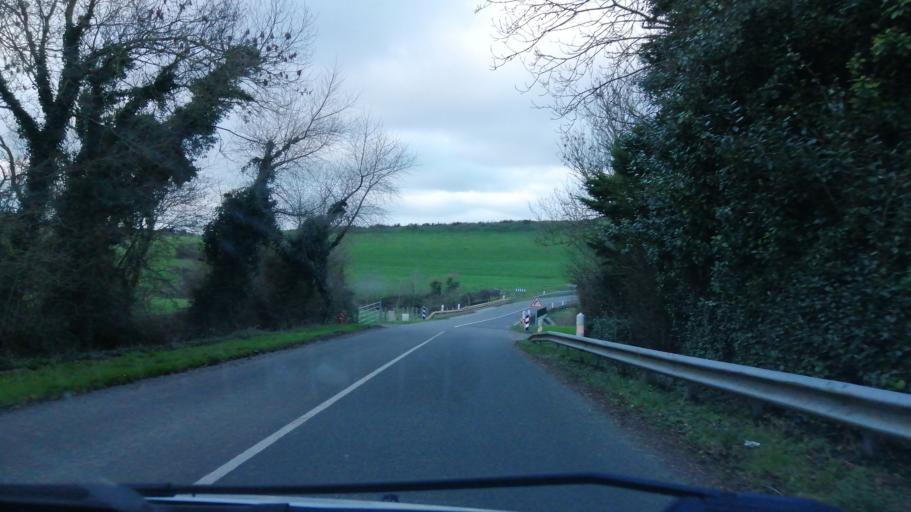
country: FR
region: Nord-Pas-de-Calais
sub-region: Departement du Pas-de-Calais
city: Wissant
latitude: 50.8591
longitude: 1.6184
